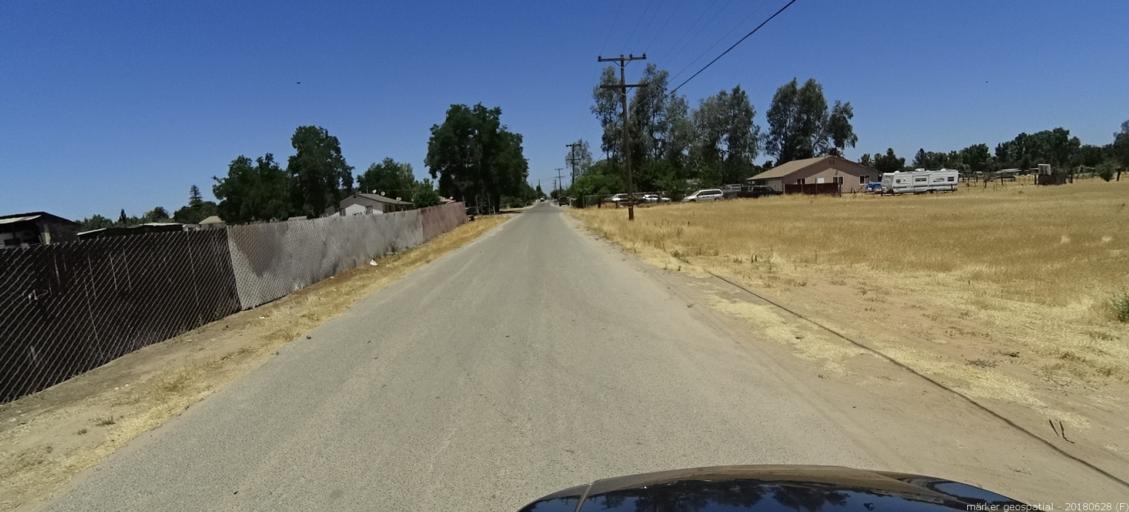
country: US
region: California
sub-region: Madera County
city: Parksdale
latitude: 36.9426
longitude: -120.0150
